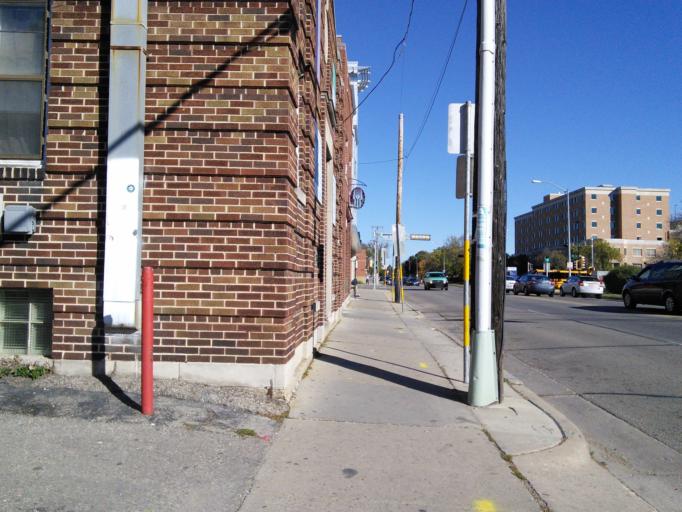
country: US
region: Wisconsin
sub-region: Dane County
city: Madison
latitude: 43.0678
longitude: -89.4020
